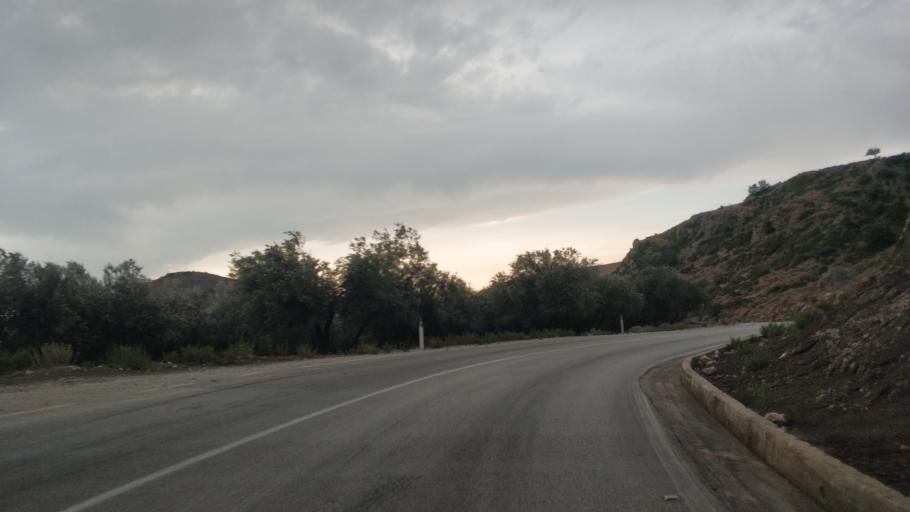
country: AL
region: Vlore
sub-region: Rrethi i Sarandes
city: Lukove
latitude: 40.0351
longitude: 19.8836
